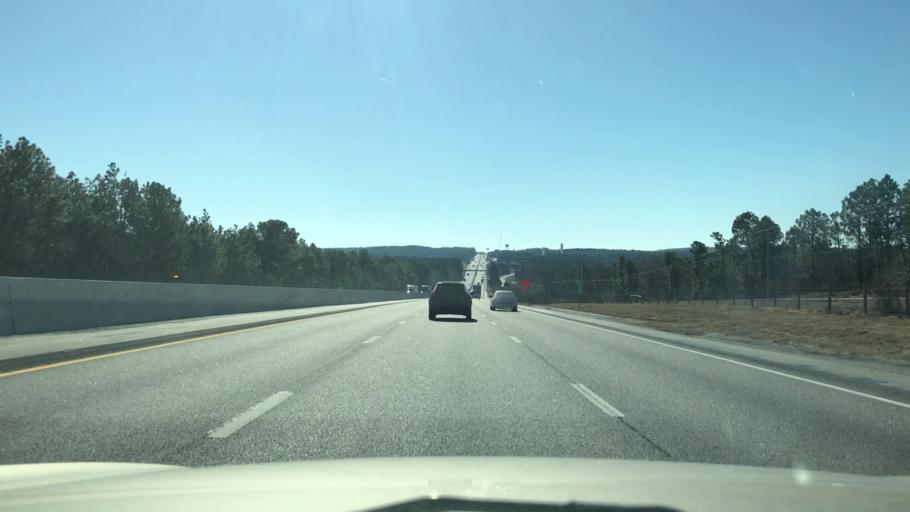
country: US
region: South Carolina
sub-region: Lexington County
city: Gaston
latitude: 33.8608
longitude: -81.0306
